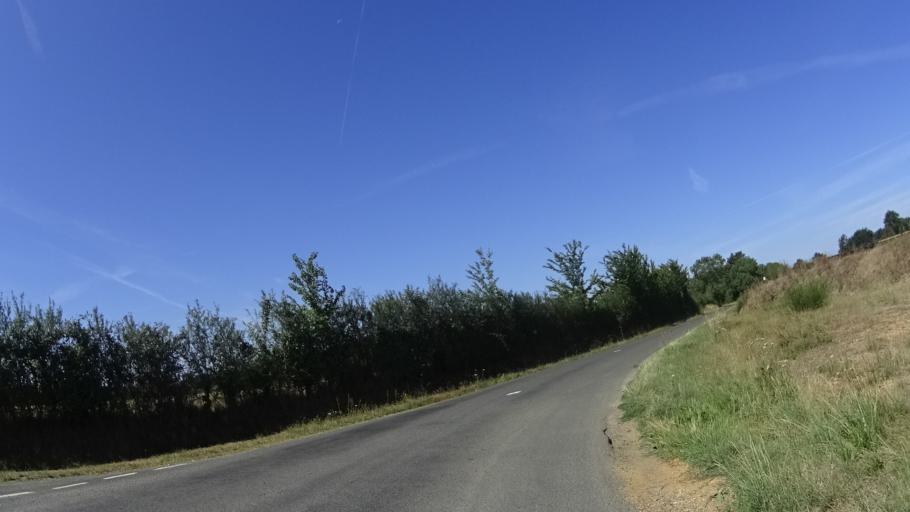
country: FR
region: Pays de la Loire
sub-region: Departement de Maine-et-Loire
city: Soulaire-et-Bourg
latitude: 47.5942
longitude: -0.5372
